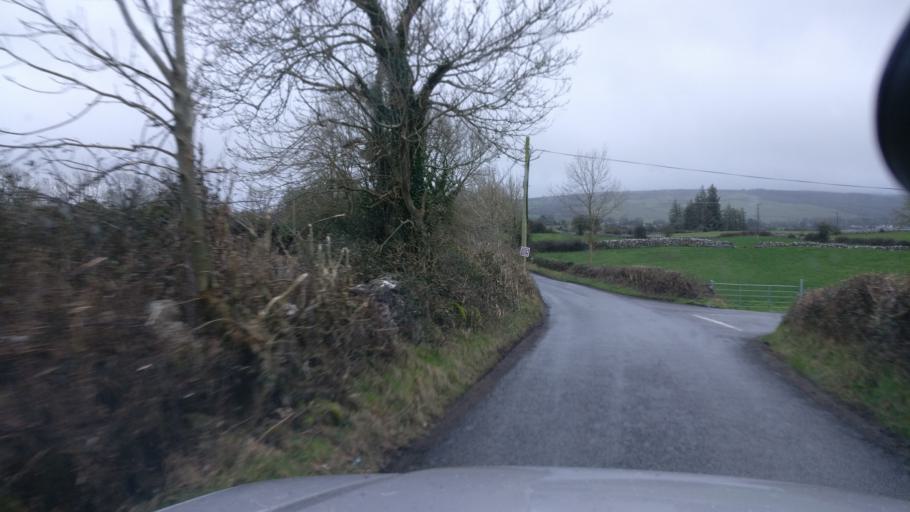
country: IE
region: Connaught
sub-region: County Galway
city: Loughrea
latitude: 53.1880
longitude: -8.6605
